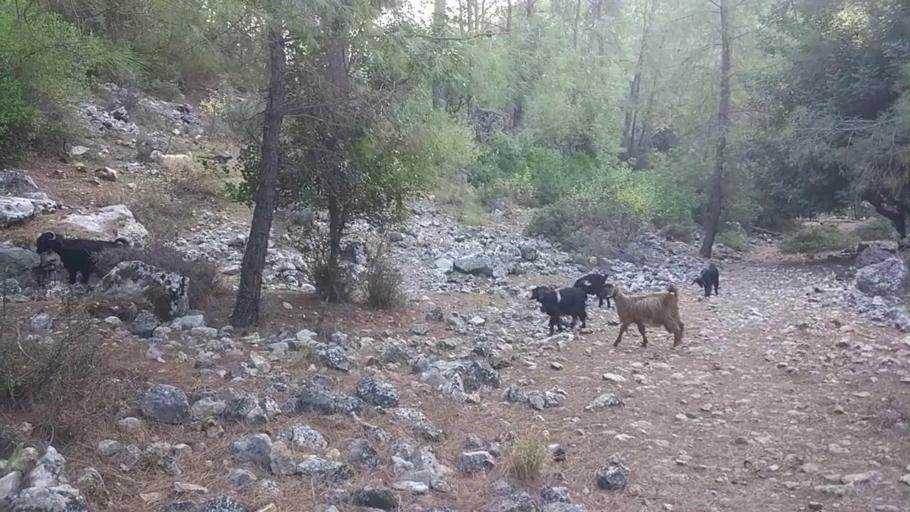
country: TR
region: Antalya
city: Tekirova
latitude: 36.4391
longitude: 30.4424
